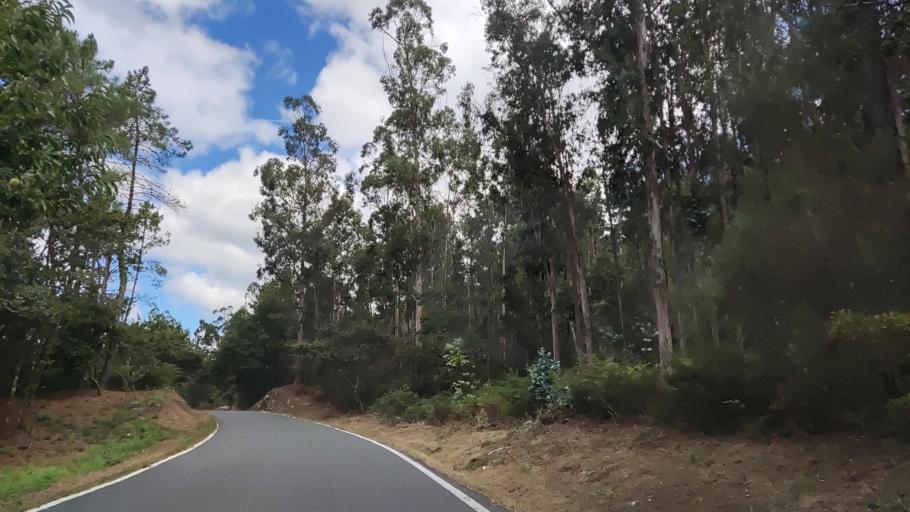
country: ES
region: Galicia
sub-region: Provincia da Coruna
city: Rois
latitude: 42.7506
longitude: -8.7016
